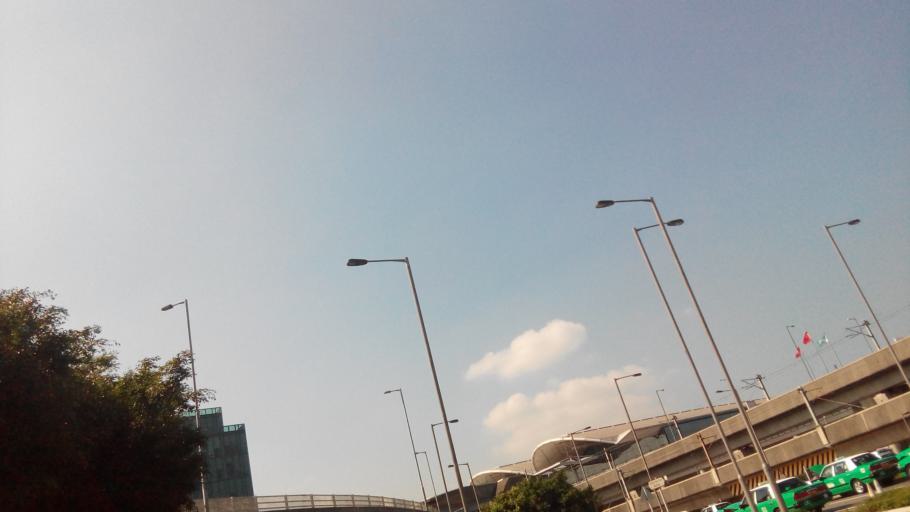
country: HK
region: Tuen Mun
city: Tuen Mun
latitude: 22.3189
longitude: 113.9364
